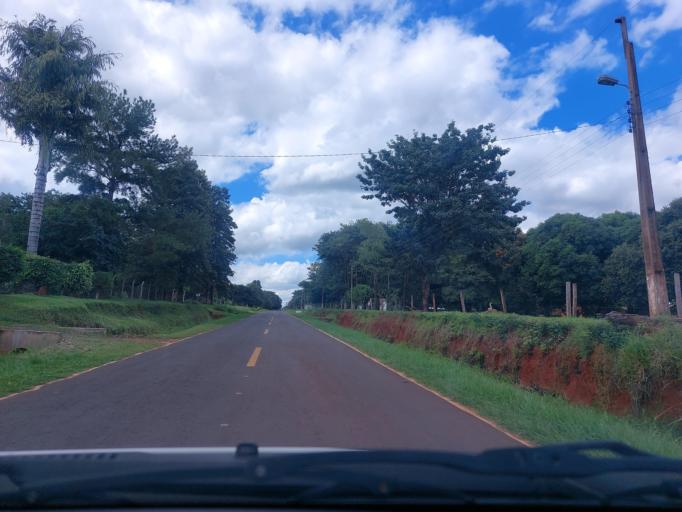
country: PY
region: San Pedro
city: Guayaybi
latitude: -24.5318
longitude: -56.5250
